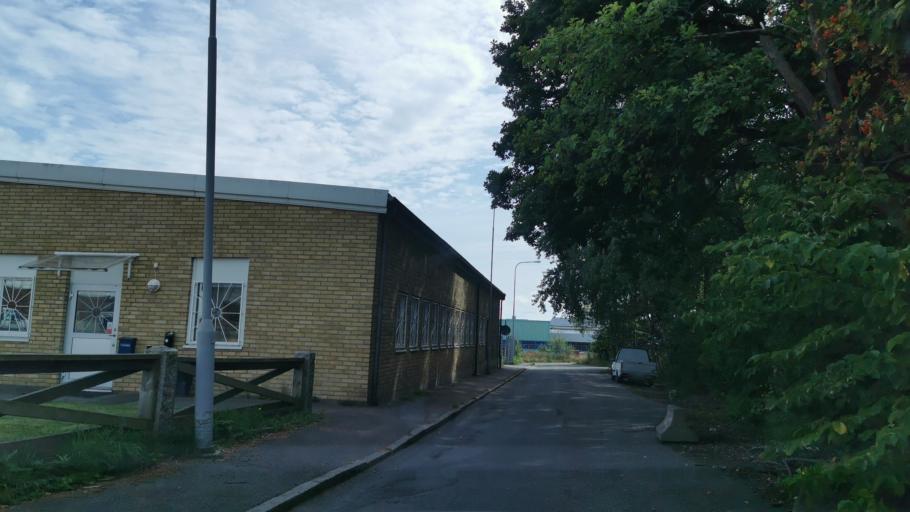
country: SE
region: Vaestra Goetaland
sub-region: Goteborg
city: Majorna
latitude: 57.6550
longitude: 11.9414
